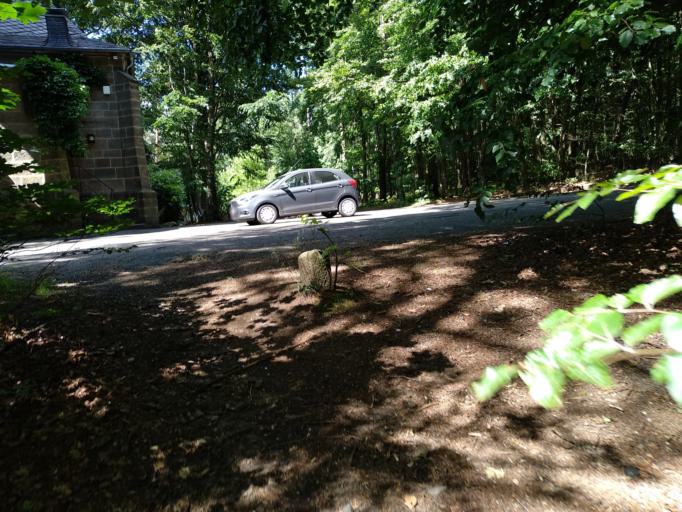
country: DE
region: Hesse
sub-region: Regierungsbezirk Giessen
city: Marburg an der Lahn
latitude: 50.8148
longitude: 8.7891
